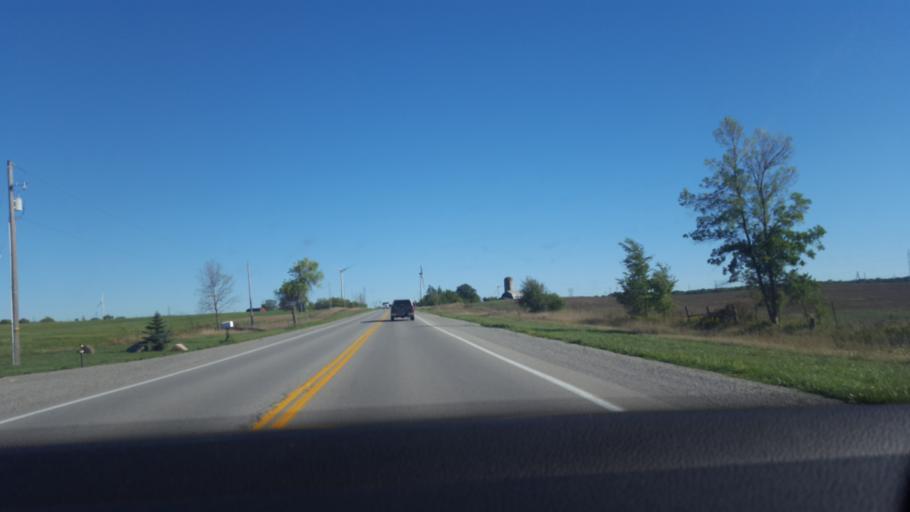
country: CA
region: Ontario
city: Welland
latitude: 43.0773
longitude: -79.5111
